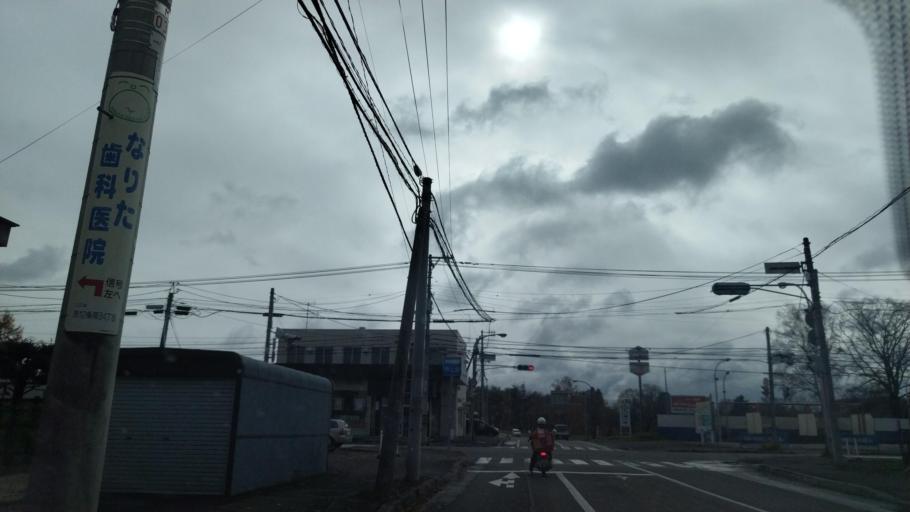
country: JP
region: Hokkaido
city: Obihiro
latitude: 42.8911
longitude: 143.1889
